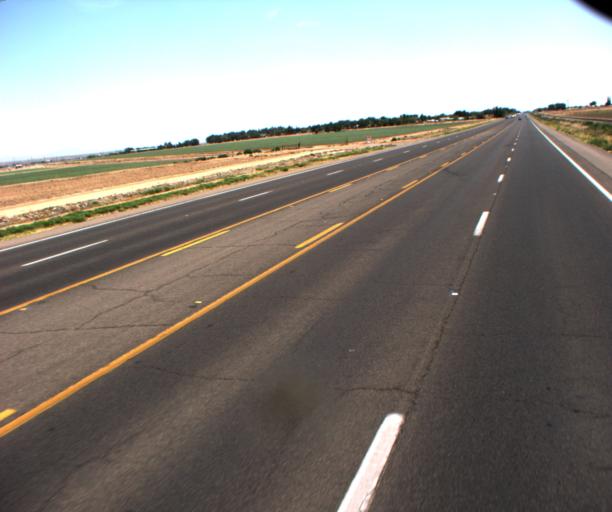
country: US
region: Arizona
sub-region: Graham County
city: Pima
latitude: 32.8791
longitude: -109.8053
